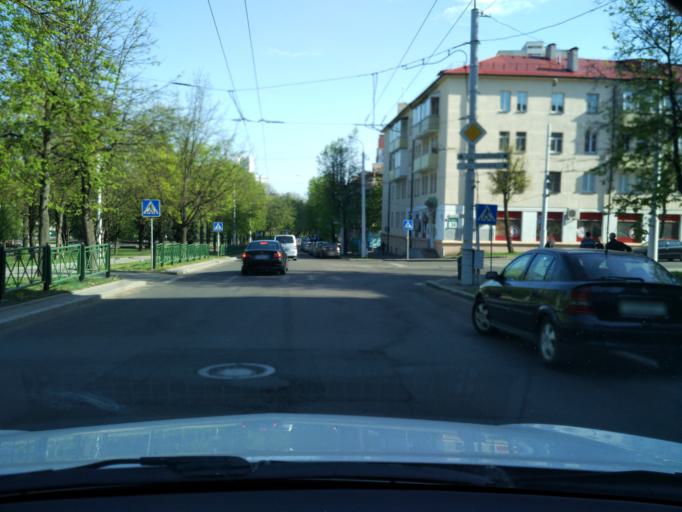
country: BY
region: Minsk
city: Minsk
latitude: 53.9294
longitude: 27.6099
